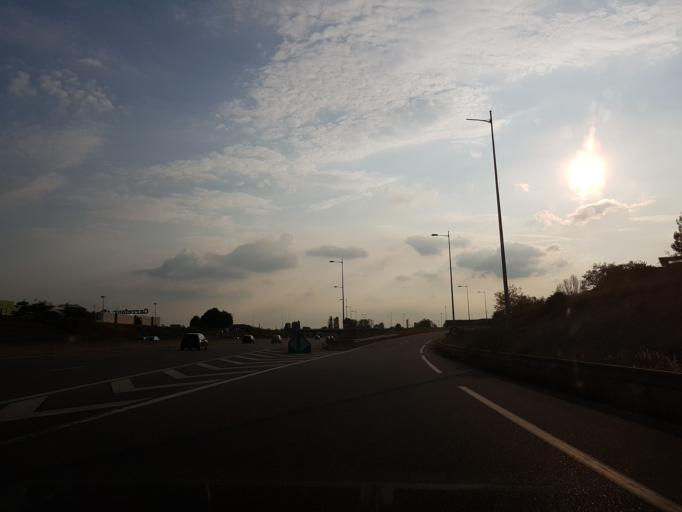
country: FR
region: Alsace
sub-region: Departement du Haut-Rhin
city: Sausheim
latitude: 47.7747
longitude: 7.3855
